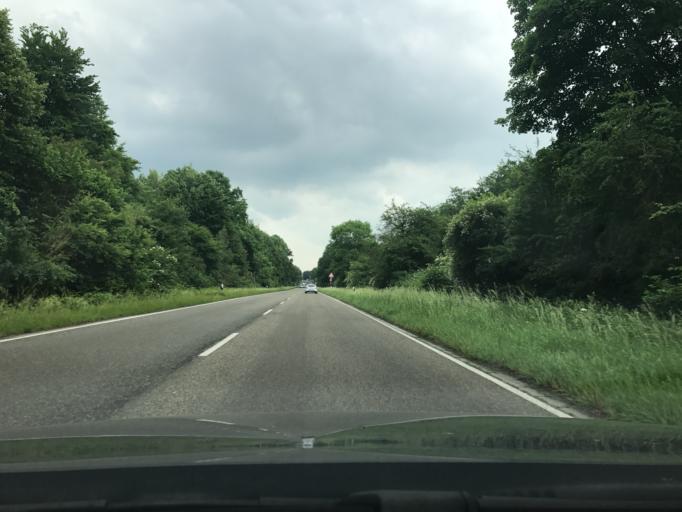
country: DE
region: North Rhine-Westphalia
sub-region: Regierungsbezirk Dusseldorf
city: Ratingen
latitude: 51.3028
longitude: 6.7944
